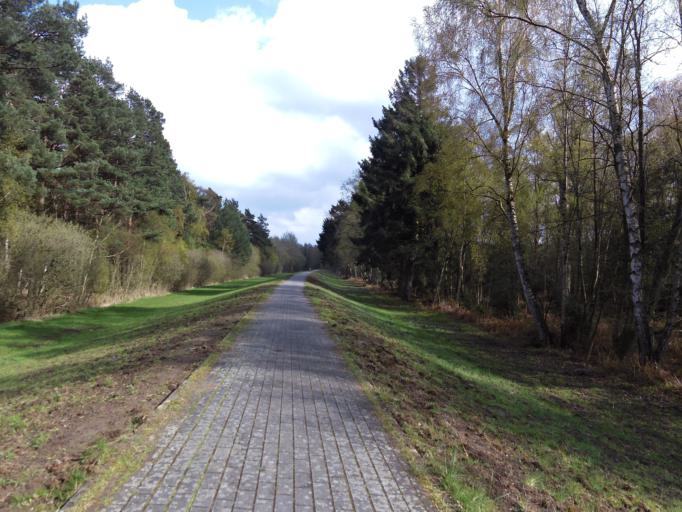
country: DE
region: Mecklenburg-Vorpommern
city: Zingst
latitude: 54.4305
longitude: 12.6654
